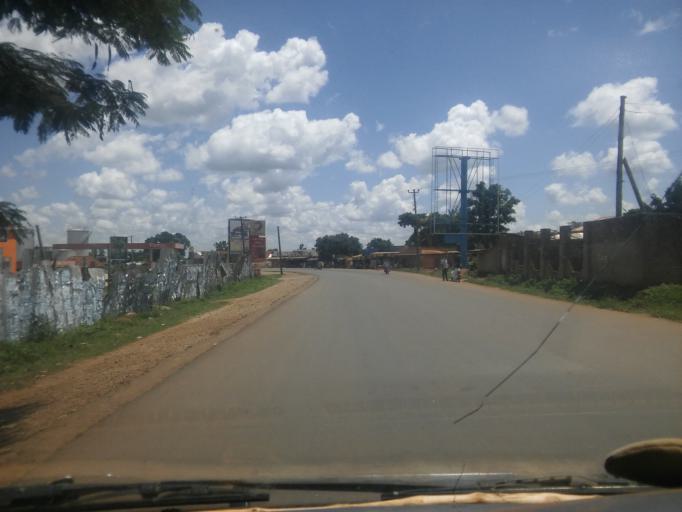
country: UG
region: Eastern Region
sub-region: Mbale District
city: Mbale
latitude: 1.0792
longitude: 34.1553
